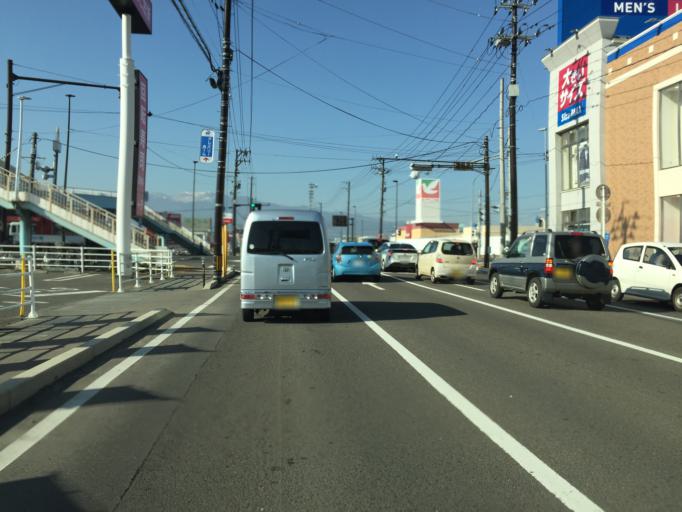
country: JP
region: Fukushima
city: Fukushima-shi
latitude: 37.7267
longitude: 140.4674
